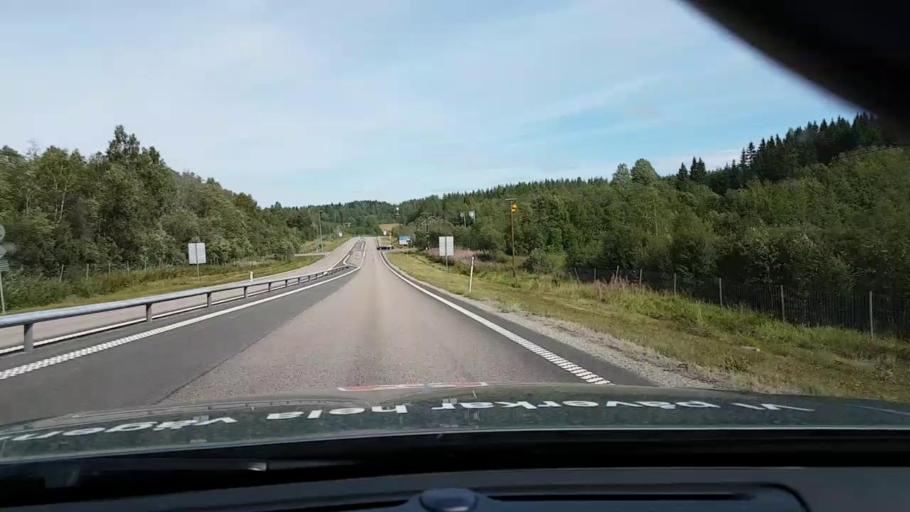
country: SE
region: Vaesternorrland
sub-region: OErnskoeldsviks Kommun
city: Ornskoldsvik
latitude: 63.3096
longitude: 18.9310
